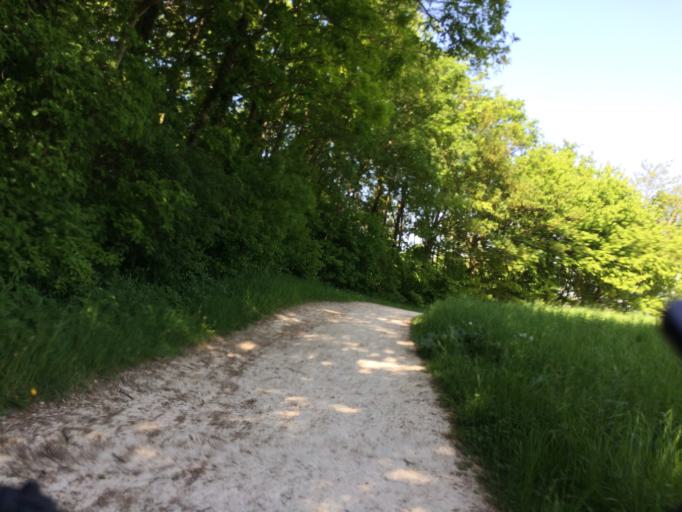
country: FR
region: Ile-de-France
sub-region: Departement des Hauts-de-Seine
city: Chatenay-Malabry
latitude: 48.7589
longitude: 2.2604
